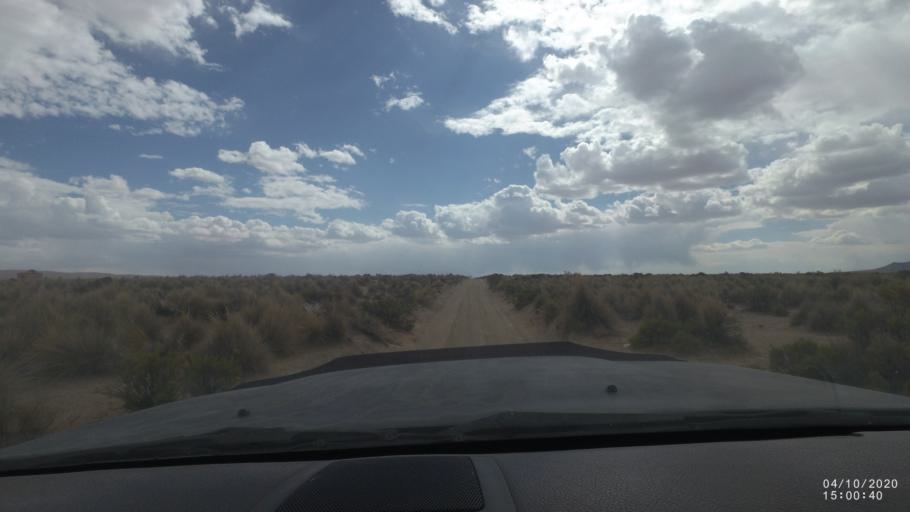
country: BO
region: Oruro
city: Poopo
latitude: -18.6866
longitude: -67.5285
